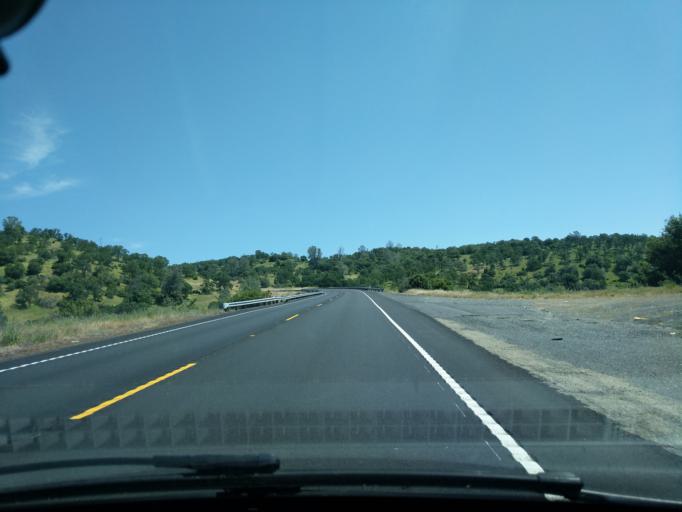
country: US
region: California
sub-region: Calaveras County
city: Copperopolis
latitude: 38.0031
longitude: -120.6482
